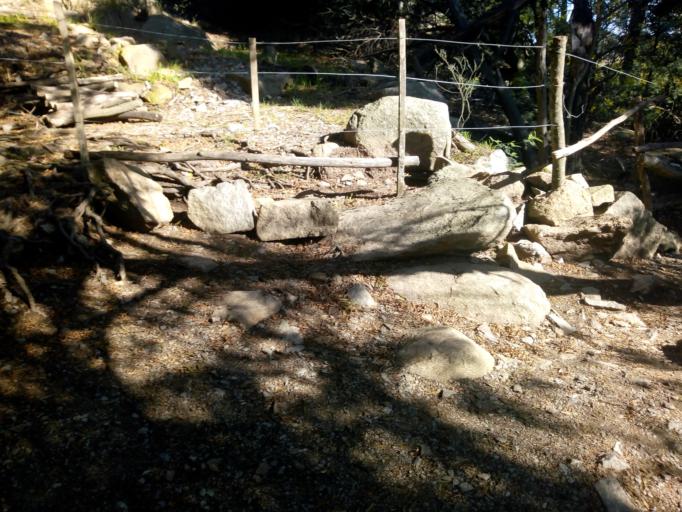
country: AR
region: Buenos Aires
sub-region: Partido de Tandil
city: Tandil
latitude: -37.3545
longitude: -59.1726
